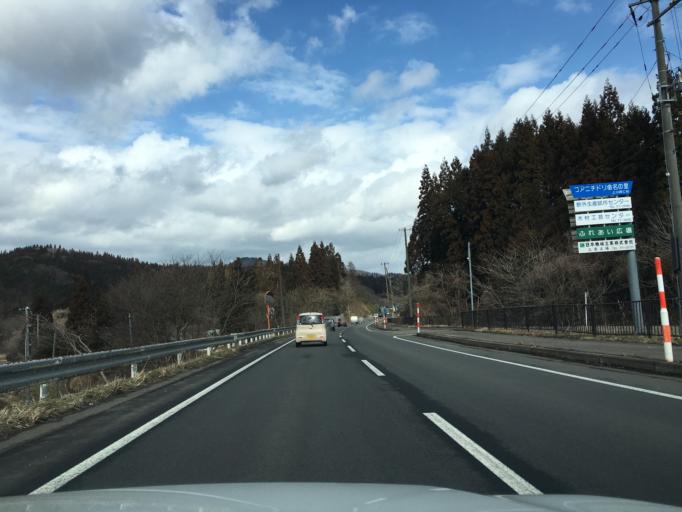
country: JP
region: Akita
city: Takanosu
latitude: 40.0266
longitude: 140.2738
